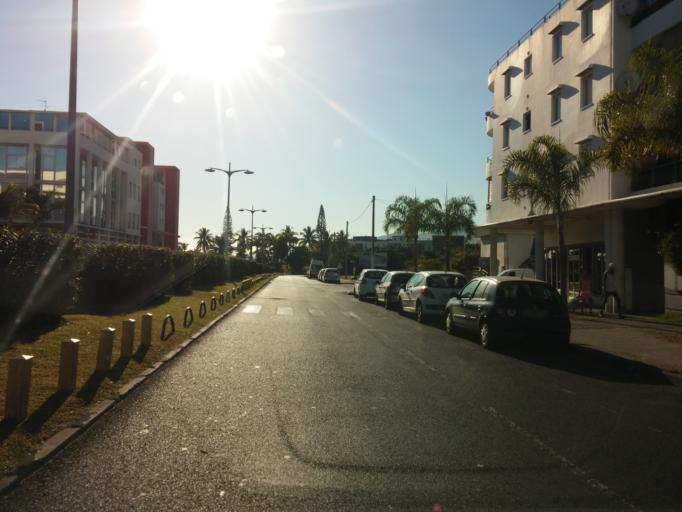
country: RE
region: Reunion
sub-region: Reunion
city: Le Port
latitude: -20.9322
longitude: 55.2954
